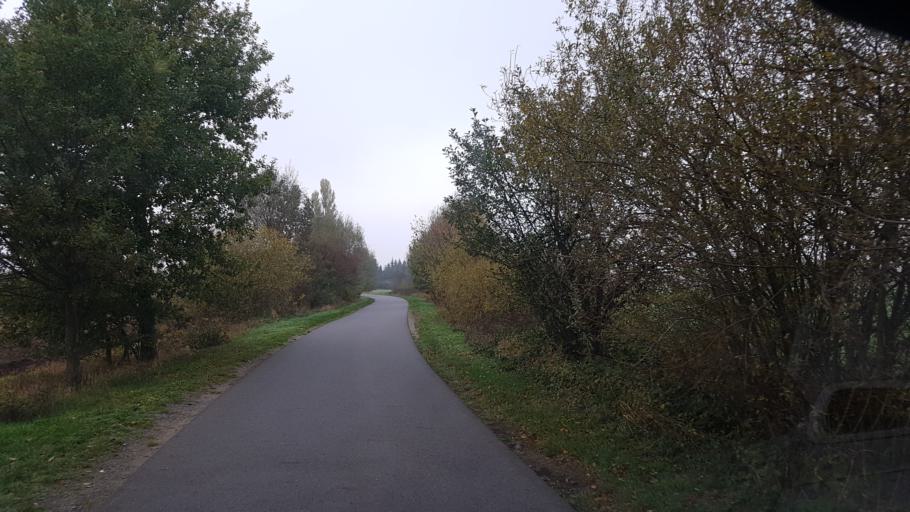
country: DE
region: Brandenburg
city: Schonewalde
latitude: 51.6785
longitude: 13.6162
